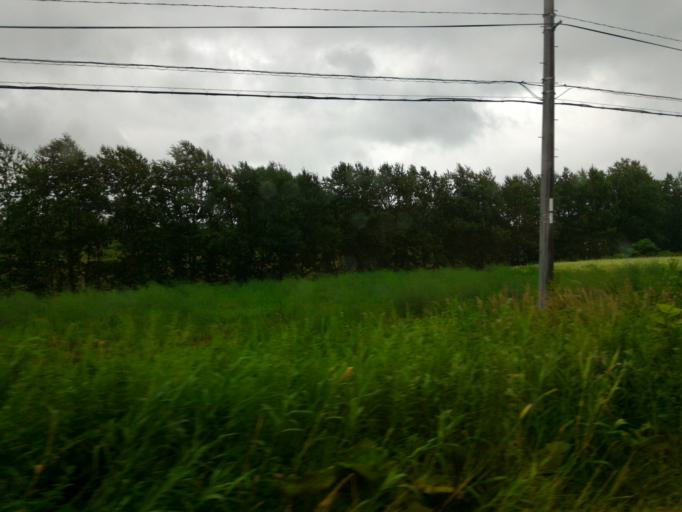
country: JP
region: Hokkaido
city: Nayoro
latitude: 44.6682
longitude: 142.2686
